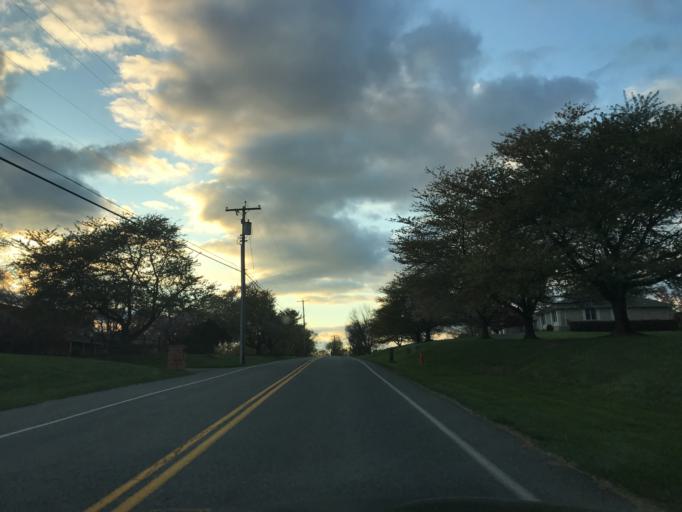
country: US
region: Maryland
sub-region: Harford County
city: Bel Air South
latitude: 39.5180
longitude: -76.2995
